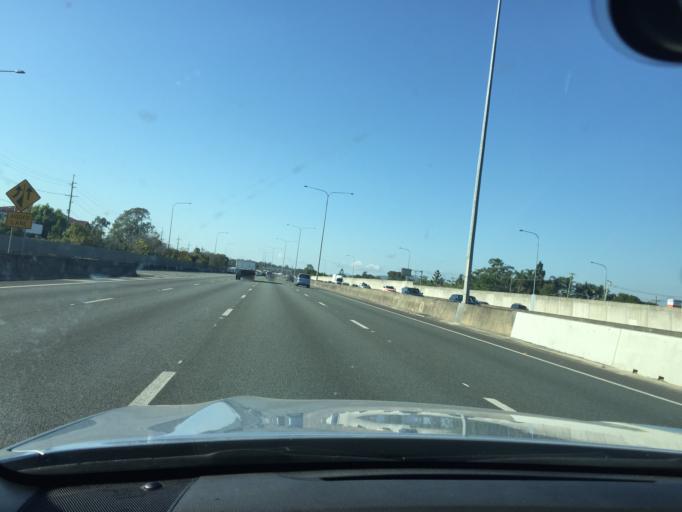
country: AU
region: Queensland
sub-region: Logan
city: Beenleigh
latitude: -27.6884
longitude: 153.1910
